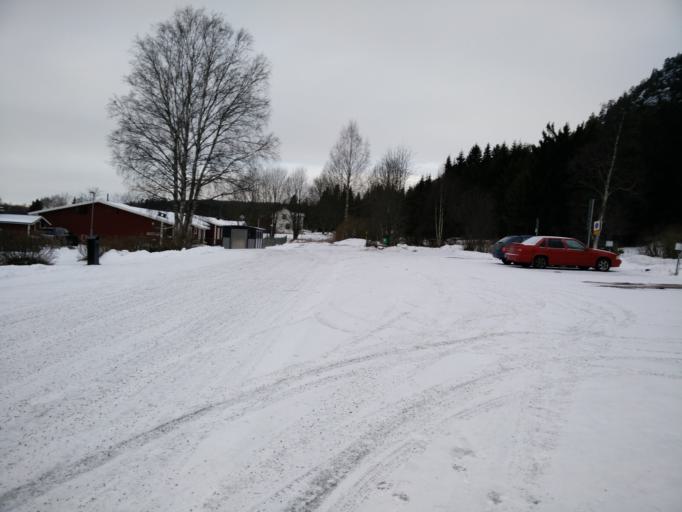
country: SE
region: Vaesternorrland
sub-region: Sundsvalls Kommun
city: Kvissleby
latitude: 62.2959
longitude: 17.3684
